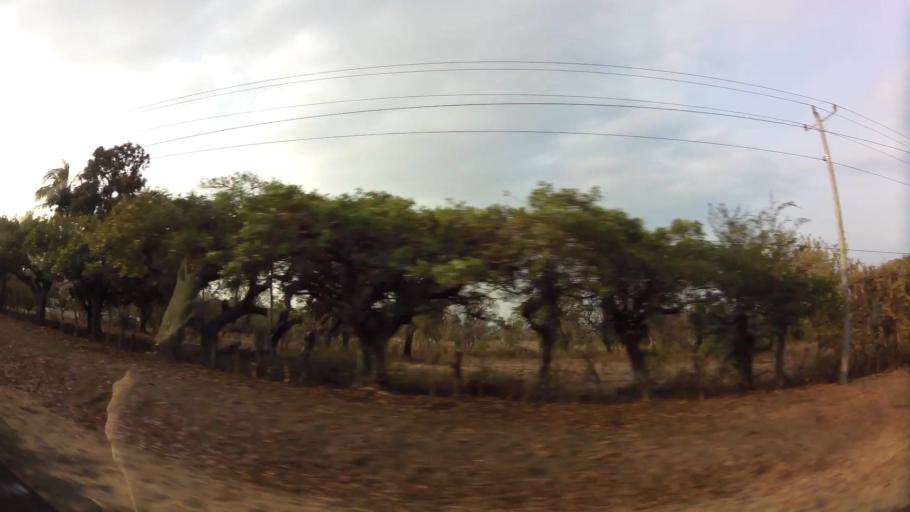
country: NI
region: Leon
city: Nagarote
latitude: 12.2742
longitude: -86.4934
